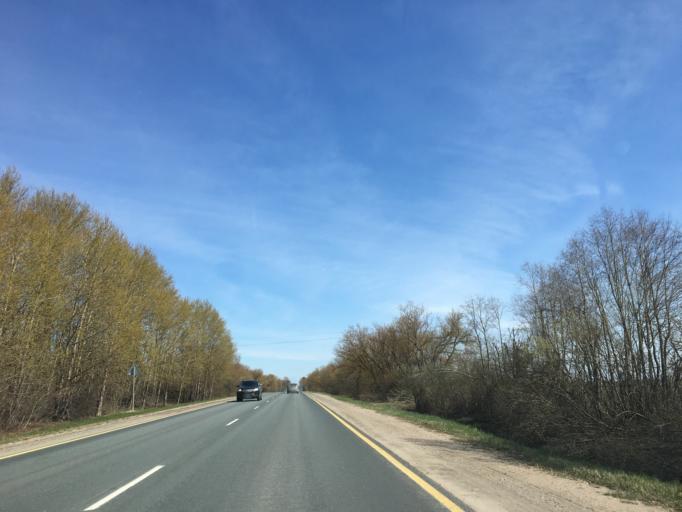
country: RU
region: Pskov
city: Izborsk
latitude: 57.7278
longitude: 27.9619
